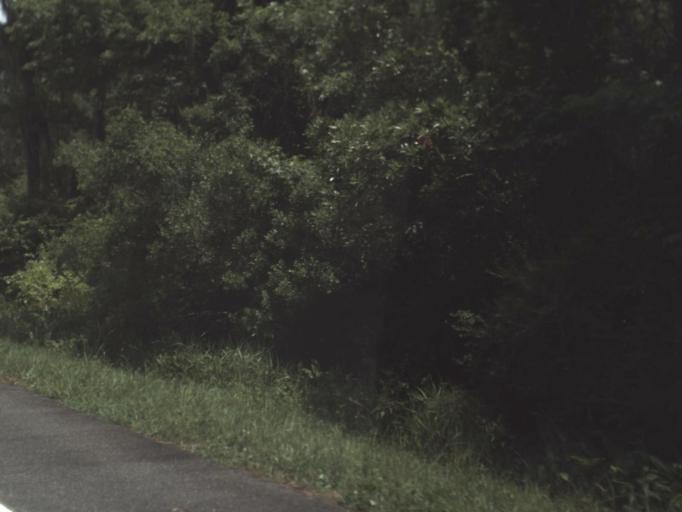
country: US
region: Florida
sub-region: Lafayette County
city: Mayo
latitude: 29.9030
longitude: -83.2947
